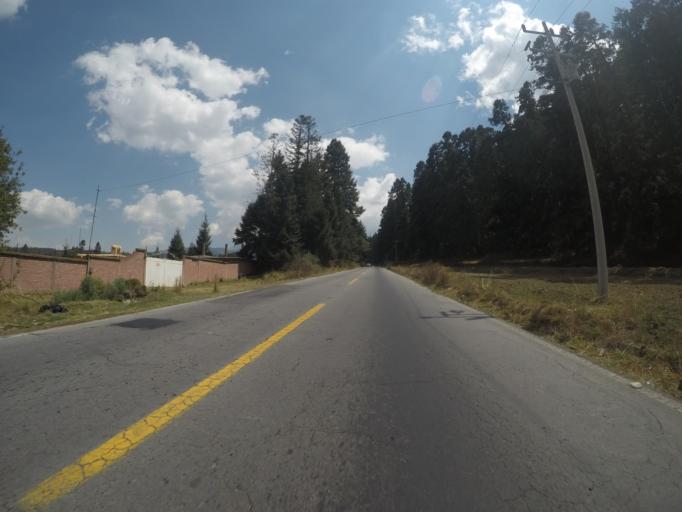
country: MX
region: Mexico
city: Cerro La Calera
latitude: 19.1951
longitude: -99.8086
